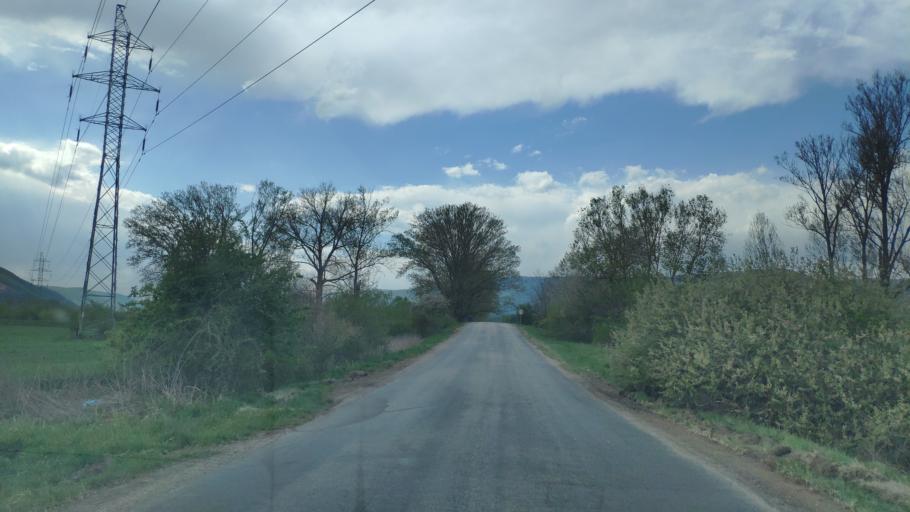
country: SK
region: Kosicky
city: Moldava nad Bodvou
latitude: 48.5933
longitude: 20.8954
